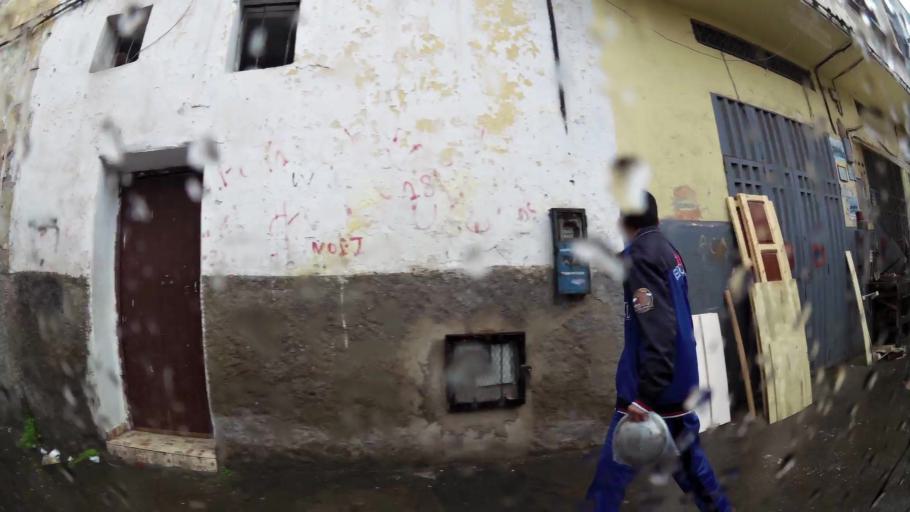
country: MA
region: Grand Casablanca
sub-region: Casablanca
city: Casablanca
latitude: 33.5746
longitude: -7.6059
